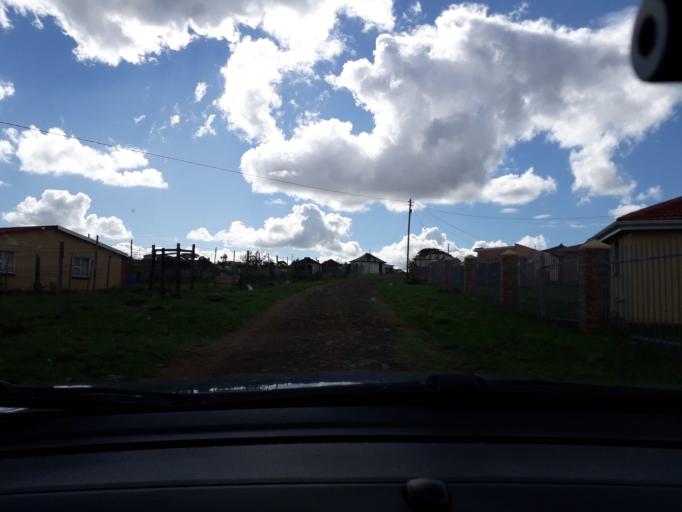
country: ZA
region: Eastern Cape
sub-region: Buffalo City Metropolitan Municipality
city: Bhisho
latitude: -33.1168
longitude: 27.4299
